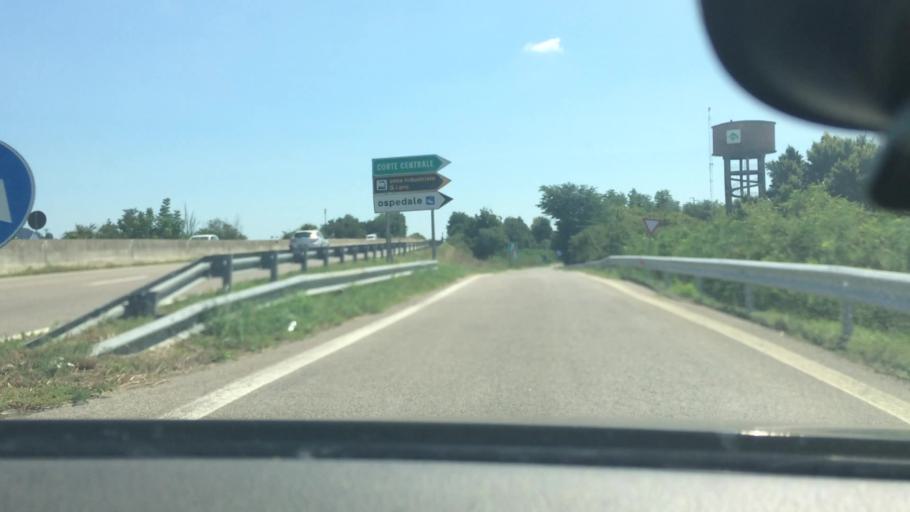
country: IT
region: Emilia-Romagna
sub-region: Provincia di Ferrara
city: Massa Fiscaglia
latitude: 44.7423
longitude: 12.0209
